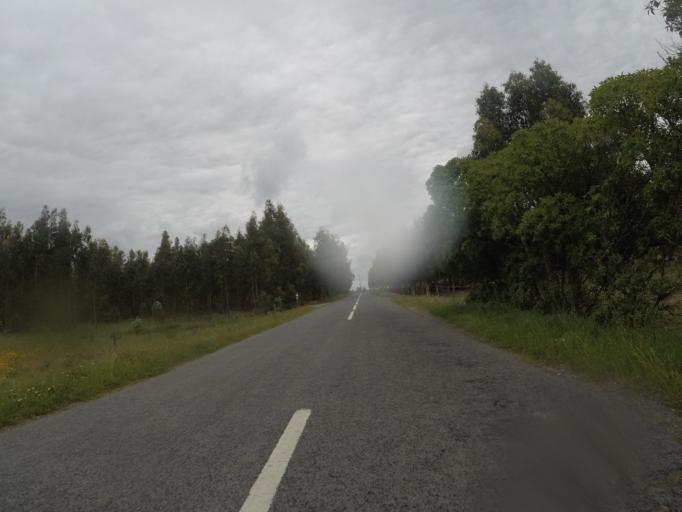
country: PT
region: Beja
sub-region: Odemira
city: Sao Teotonio
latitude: 37.5961
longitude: -8.7733
